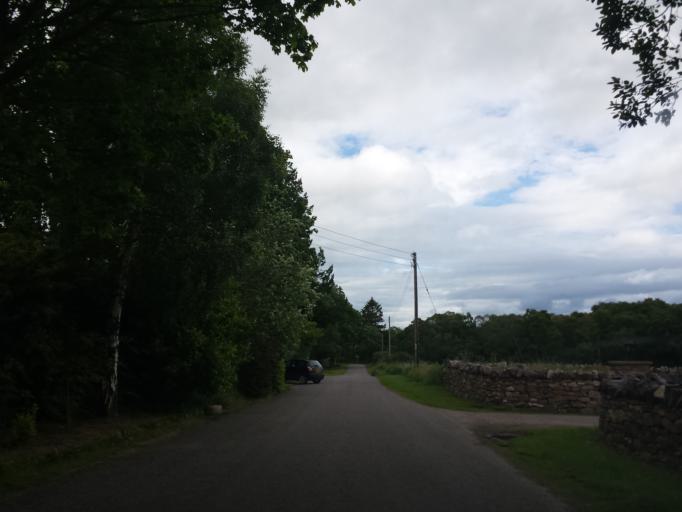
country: GB
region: Scotland
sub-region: Highland
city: Fortrose
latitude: 57.5116
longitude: -4.0219
